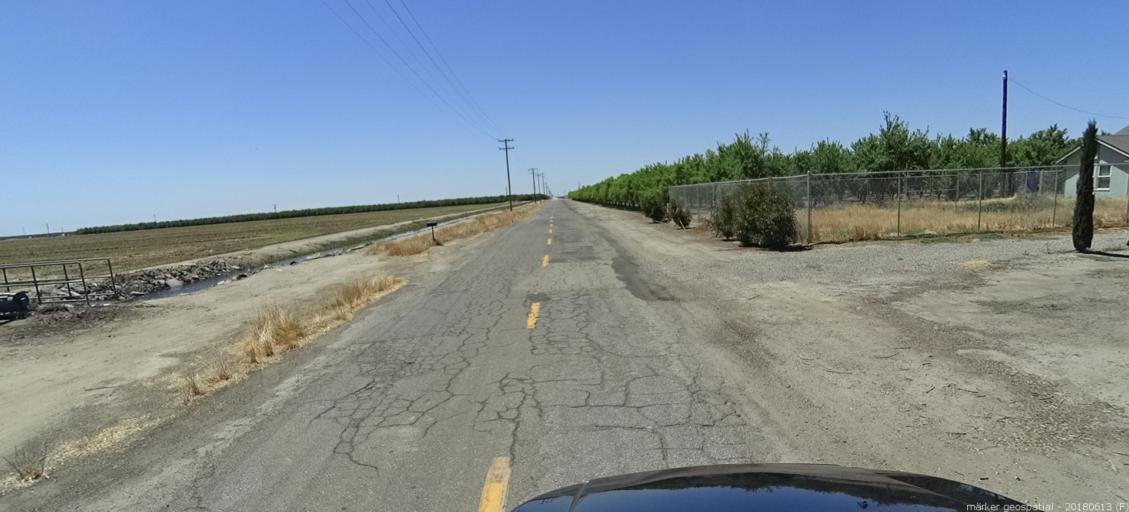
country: US
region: California
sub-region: Madera County
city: Chowchilla
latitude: 37.0146
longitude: -120.3105
